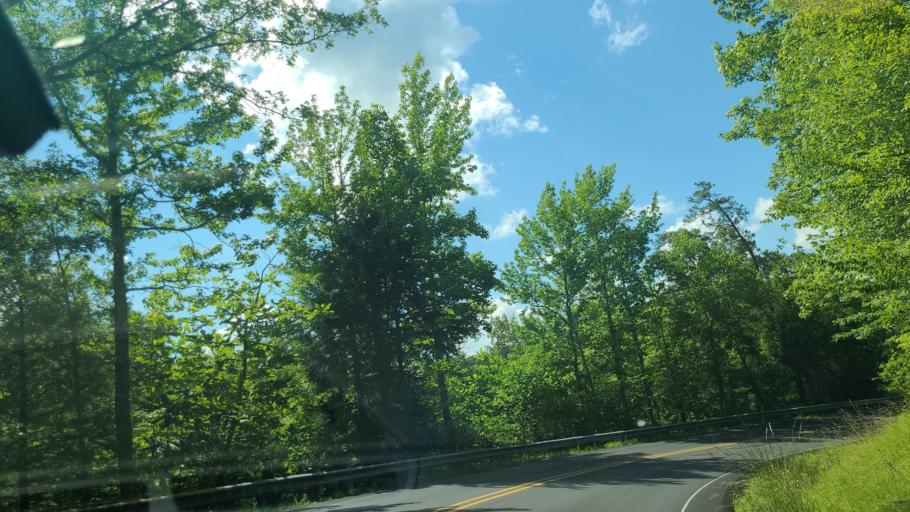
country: US
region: Kentucky
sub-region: McCreary County
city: Whitley City
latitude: 36.8392
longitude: -84.3421
